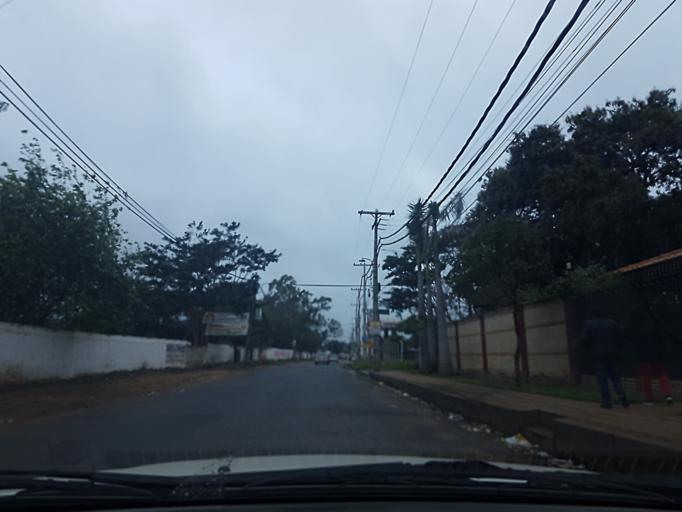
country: PY
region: Central
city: San Lorenzo
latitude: -25.2709
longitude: -57.4769
